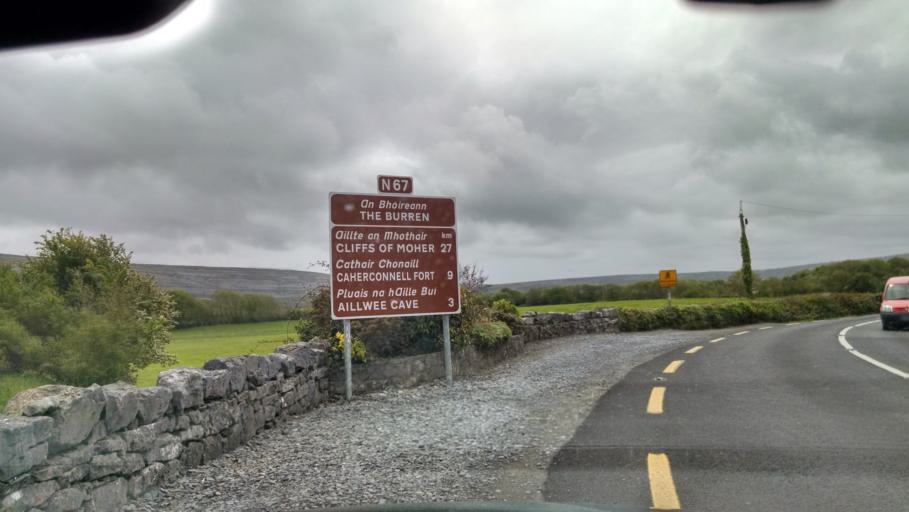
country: IE
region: Connaught
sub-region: County Galway
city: Bearna
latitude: 53.1115
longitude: -9.1511
